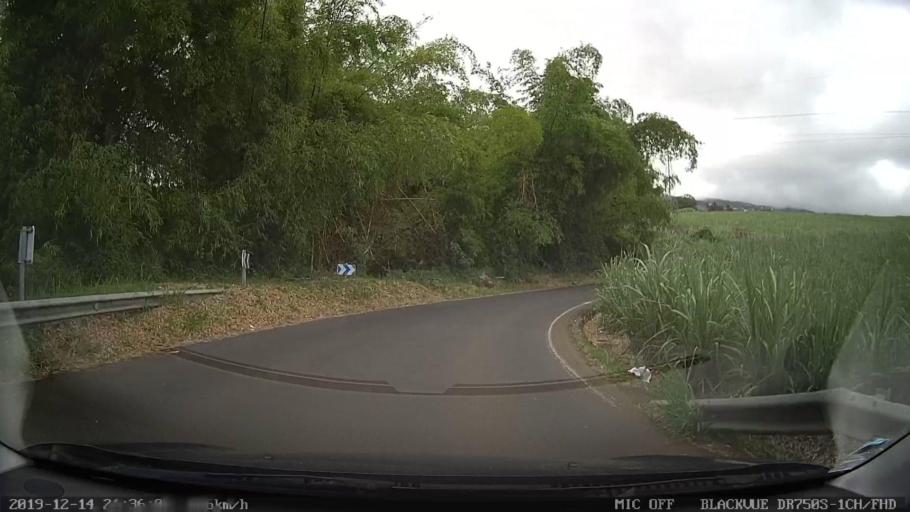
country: RE
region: Reunion
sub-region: Reunion
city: Sainte-Marie
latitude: -20.9295
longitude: 55.5365
